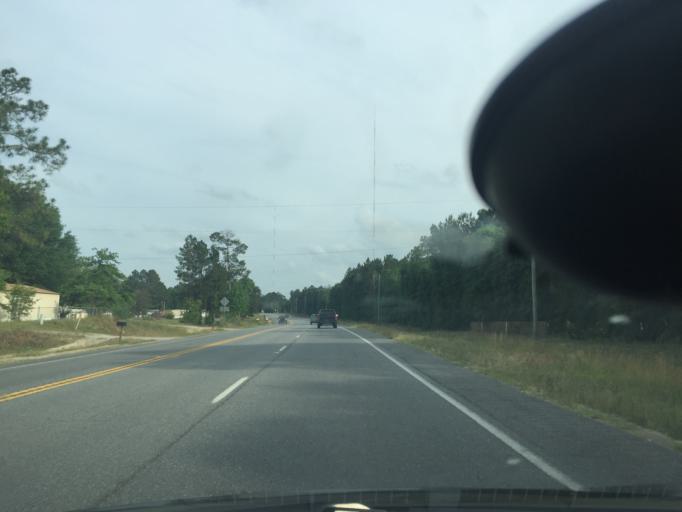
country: US
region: Georgia
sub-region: Chatham County
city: Bloomingdale
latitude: 32.0646
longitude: -81.3561
